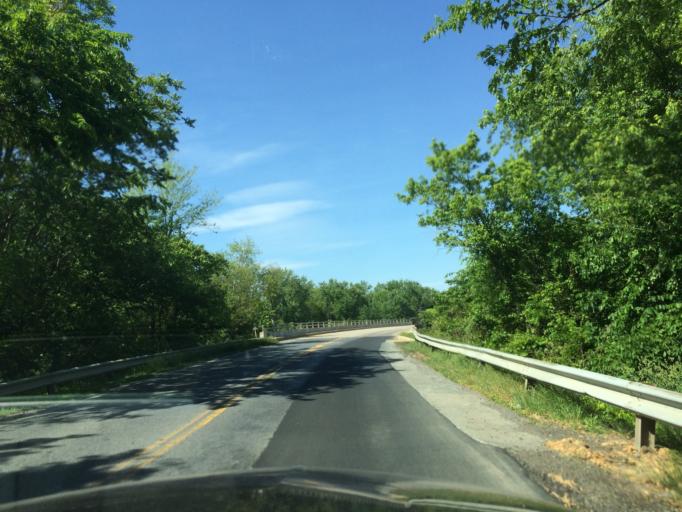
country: US
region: Maryland
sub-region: Frederick County
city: Frederick
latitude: 39.4322
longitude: -77.3800
